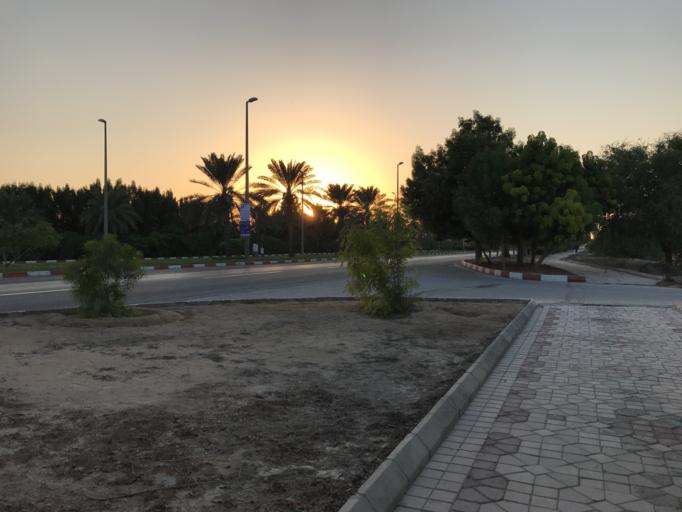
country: IR
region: Hormozgan
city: Kish
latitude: 26.5584
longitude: 54.0059
